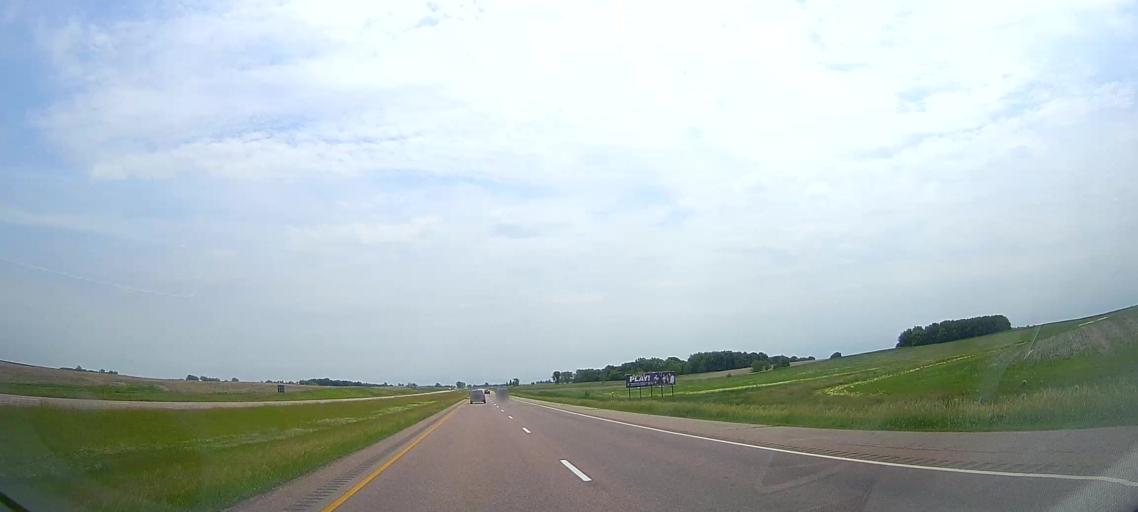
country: US
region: South Dakota
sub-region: Minnehaha County
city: Hartford
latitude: 43.6267
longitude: -97.0605
